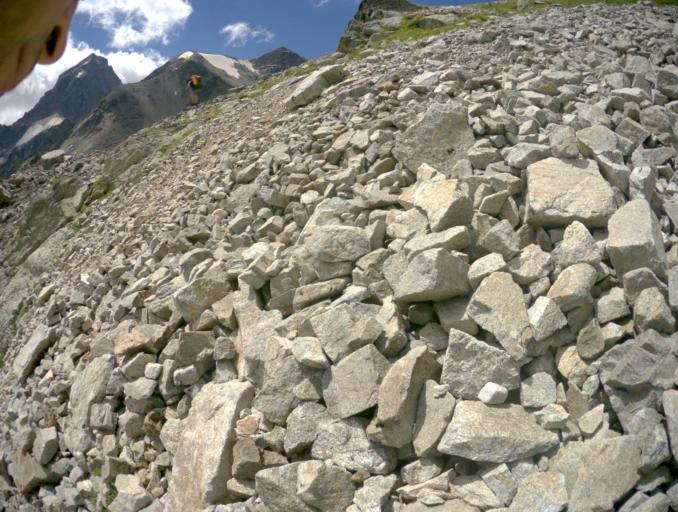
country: RU
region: Karachayevo-Cherkesiya
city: Uchkulan
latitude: 43.3240
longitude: 42.0887
